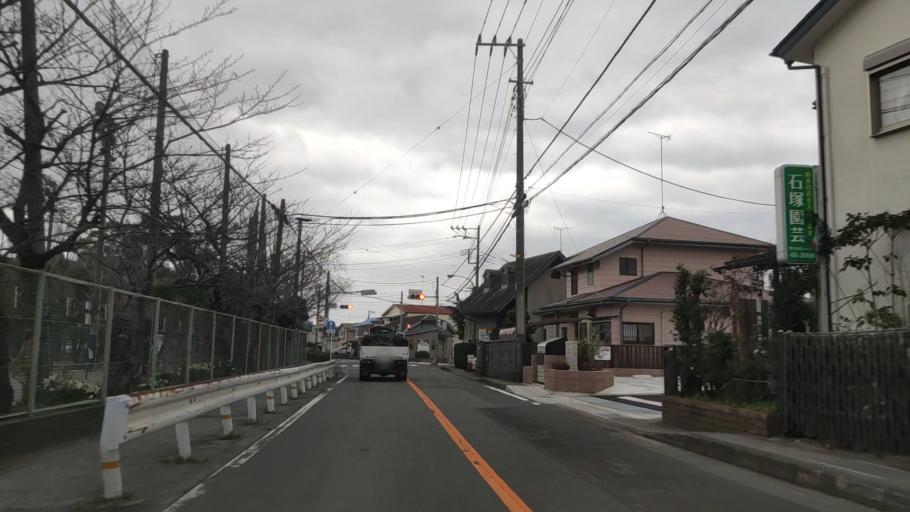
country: JP
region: Kanagawa
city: Odawara
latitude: 35.2818
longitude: 139.2017
